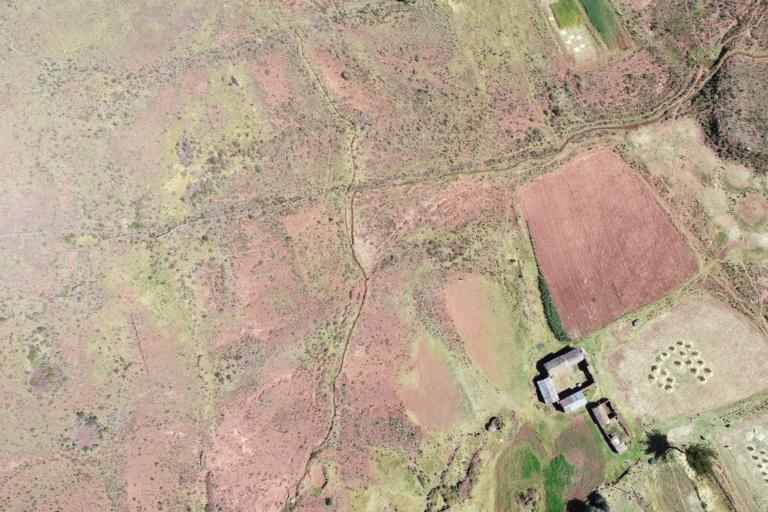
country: BO
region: La Paz
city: Tiahuanaco
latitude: -16.6077
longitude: -68.7709
